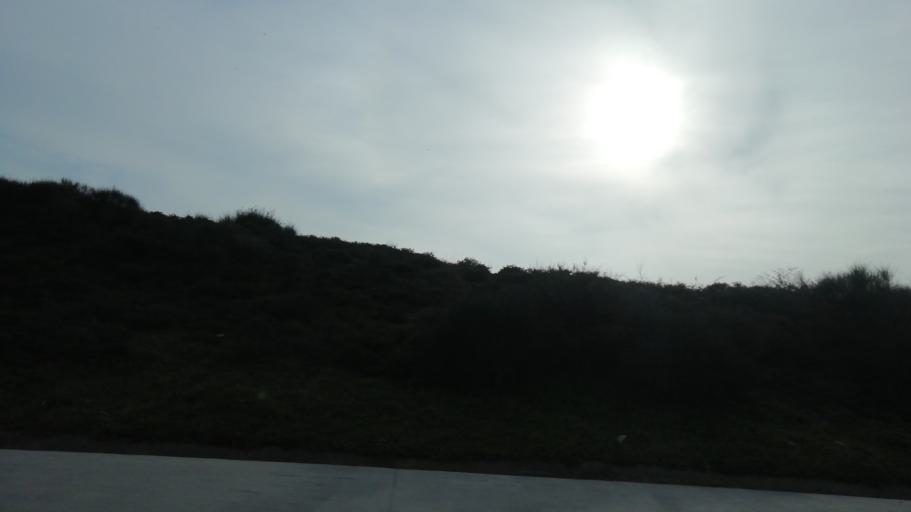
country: TR
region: Istanbul
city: Basaksehir
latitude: 41.1070
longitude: 28.7974
